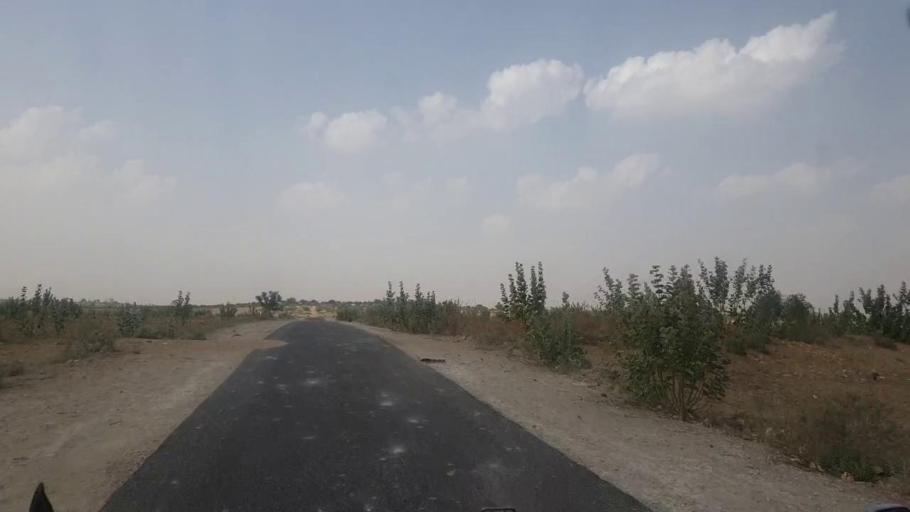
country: PK
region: Sindh
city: Islamkot
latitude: 25.2271
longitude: 70.2869
